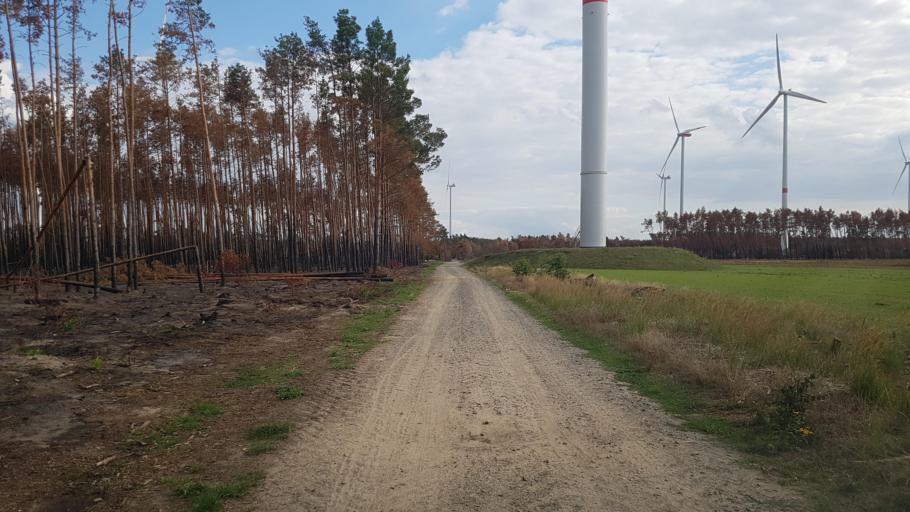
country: DE
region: Saxony
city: Arzberg
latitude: 51.5706
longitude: 13.1788
